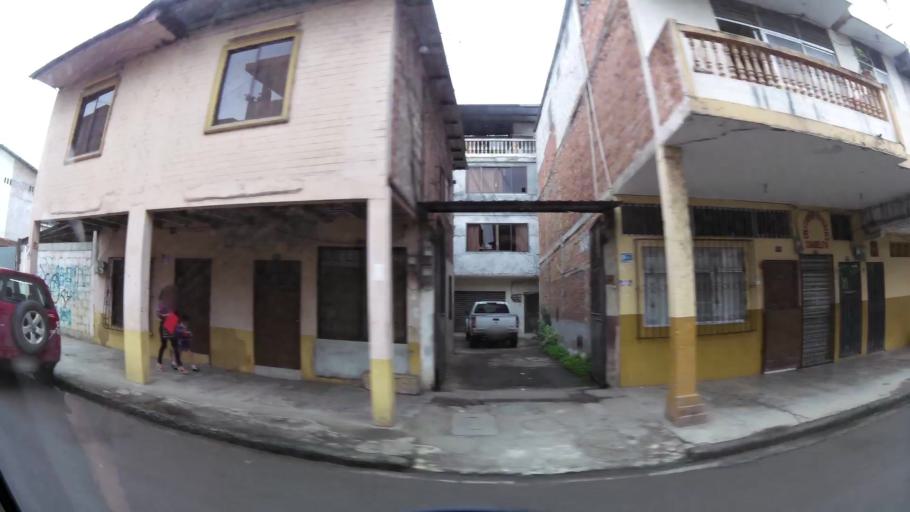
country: EC
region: El Oro
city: Pasaje
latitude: -3.3284
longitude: -79.8055
